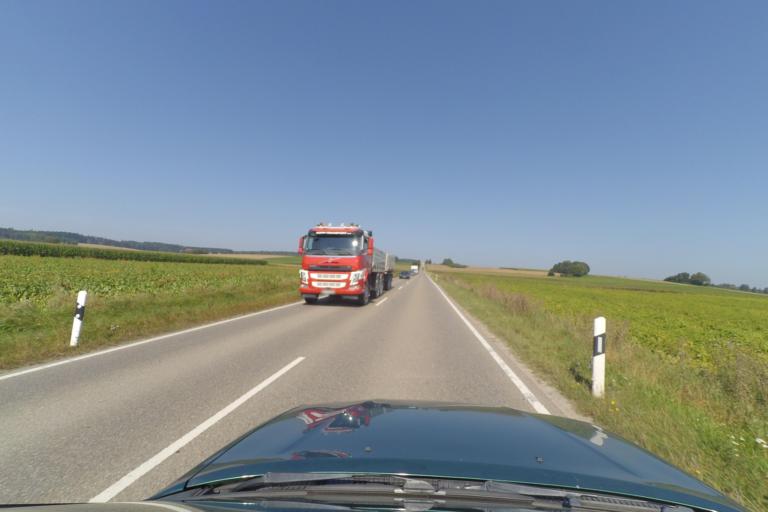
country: DE
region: Bavaria
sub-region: Swabia
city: Wittislingen
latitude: 48.6006
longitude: 10.4072
